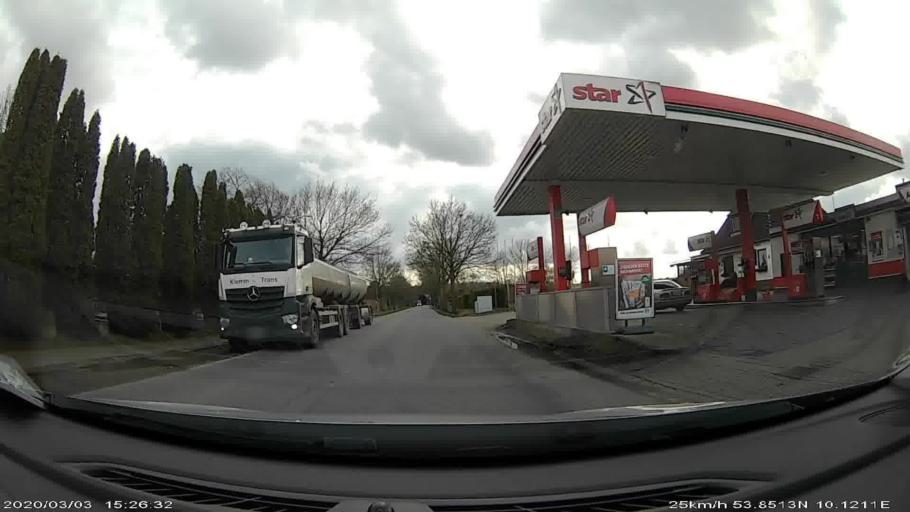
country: DE
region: Schleswig-Holstein
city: Stuvenborn
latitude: 53.8515
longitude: 10.1210
